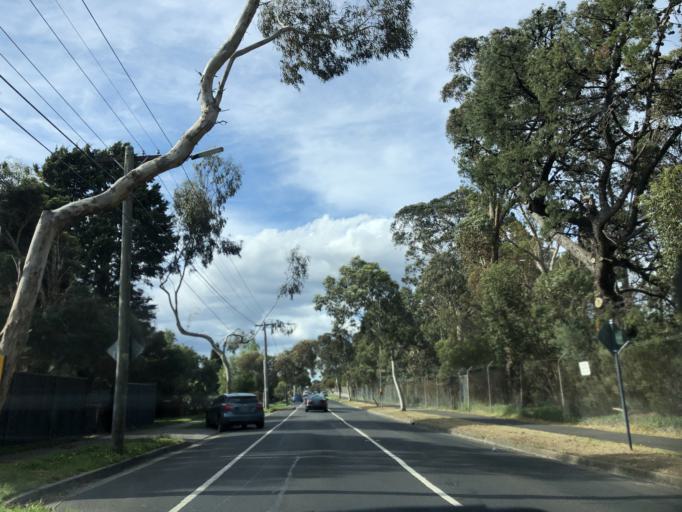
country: AU
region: Victoria
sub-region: Monash
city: Oakleigh South
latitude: -37.9140
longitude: 145.0889
